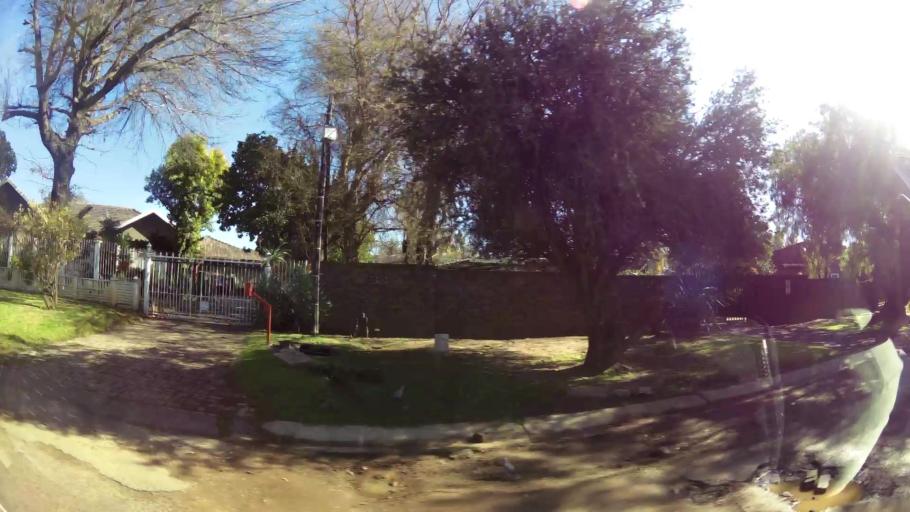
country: ZA
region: Mpumalanga
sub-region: Nkangala District Municipality
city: Witbank
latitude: -25.8811
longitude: 29.2378
